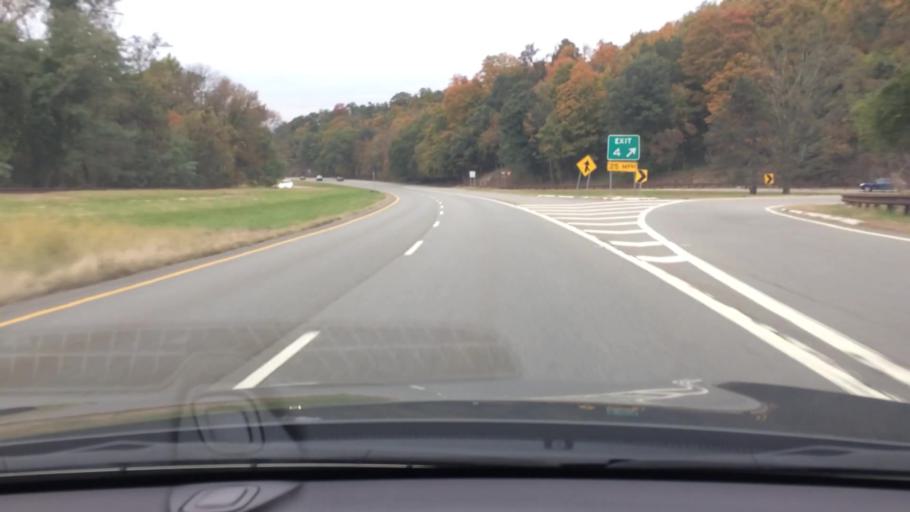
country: US
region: New York
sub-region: Westchester County
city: Hastings-on-Hudson
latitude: 40.9978
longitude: -73.9140
